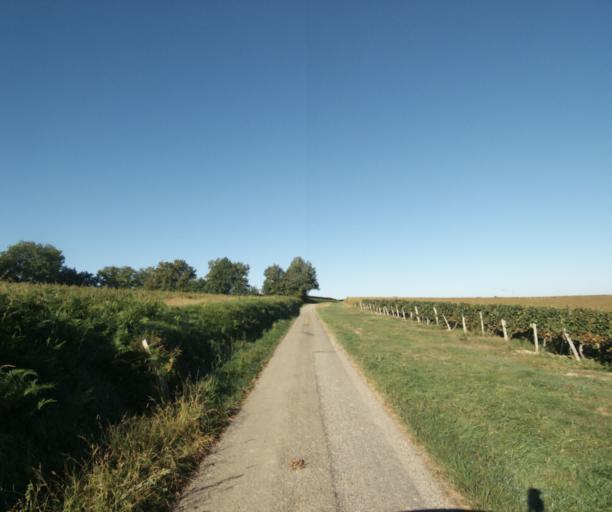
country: FR
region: Midi-Pyrenees
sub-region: Departement du Gers
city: Gondrin
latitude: 43.8367
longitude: 0.2252
